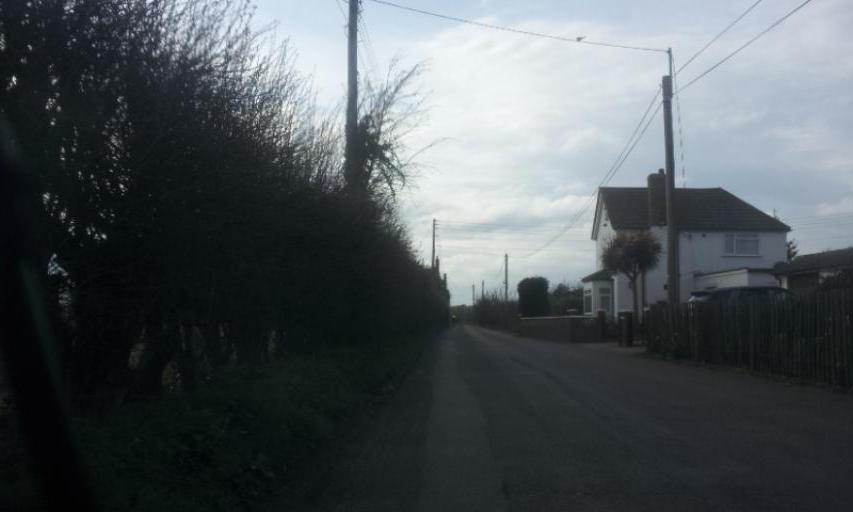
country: GB
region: England
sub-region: Kent
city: Teynham
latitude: 51.3357
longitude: 0.7978
